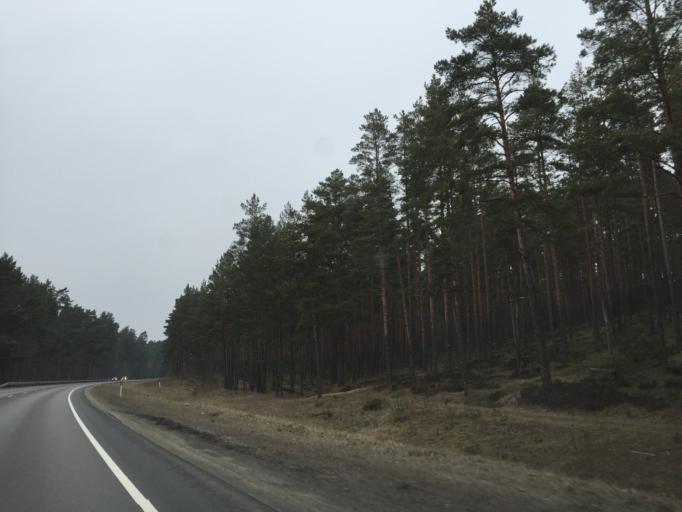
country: EE
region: Paernumaa
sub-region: Paernu linn
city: Parnu
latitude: 58.1475
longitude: 24.5021
